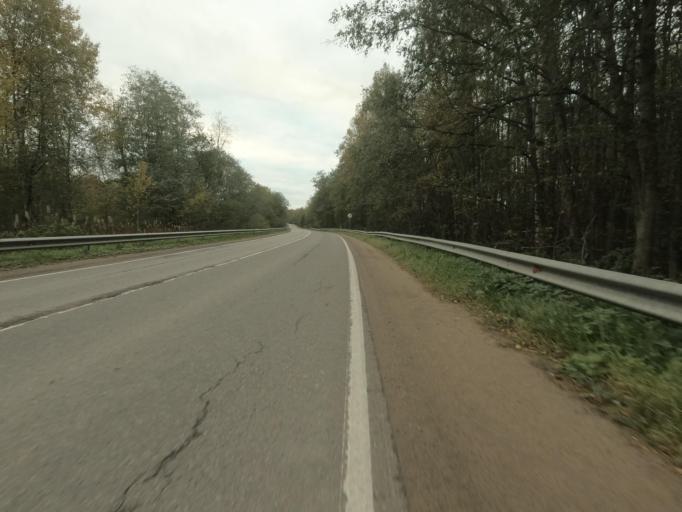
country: RU
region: Leningrad
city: Pavlovo
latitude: 59.7922
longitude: 30.9587
